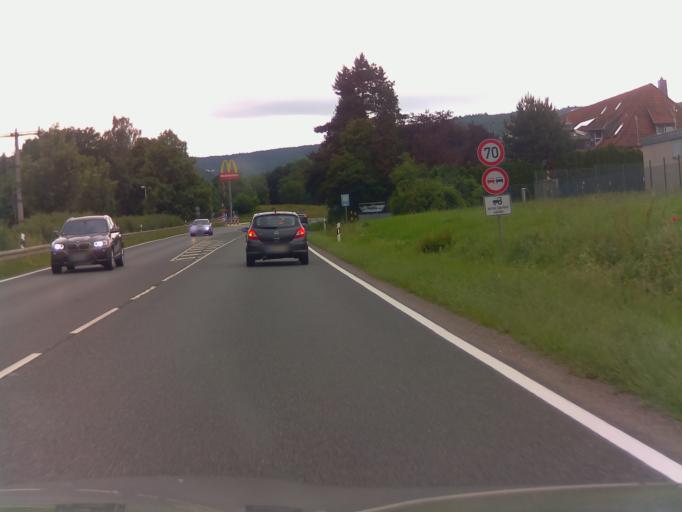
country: DE
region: Bavaria
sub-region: Regierungsbezirk Unterfranken
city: Lohr am Main
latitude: 50.0032
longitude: 9.5878
